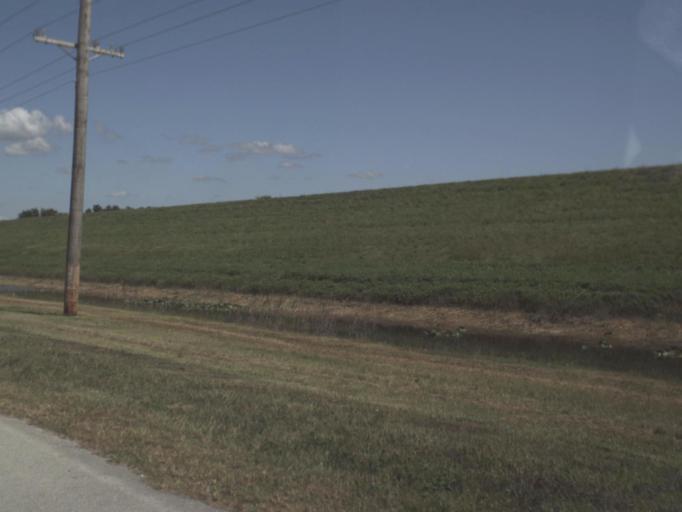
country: US
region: Florida
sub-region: Glades County
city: Moore Haven
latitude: 26.9116
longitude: -81.1224
